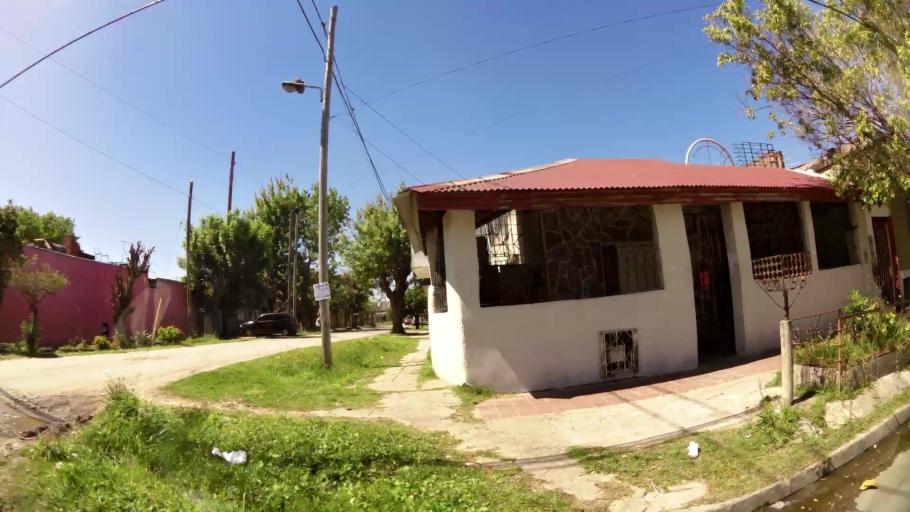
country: AR
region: Buenos Aires
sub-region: Partido de Quilmes
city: Quilmes
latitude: -34.7291
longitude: -58.3065
